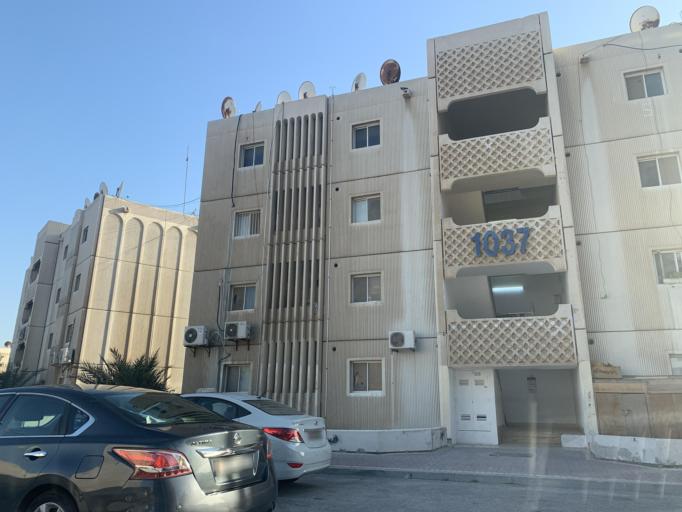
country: BH
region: Manama
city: Manama
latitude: 26.2028
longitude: 50.5843
